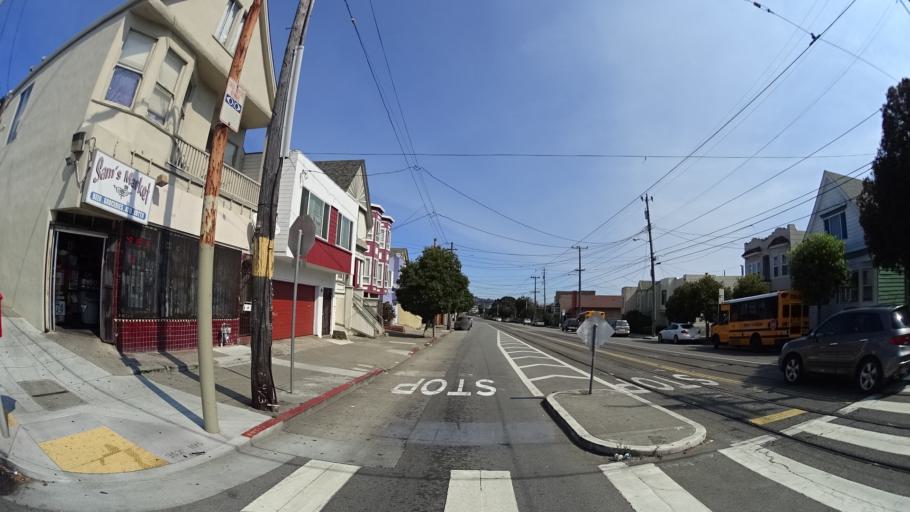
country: US
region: California
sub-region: San Mateo County
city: Daly City
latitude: 37.7163
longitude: -122.4505
